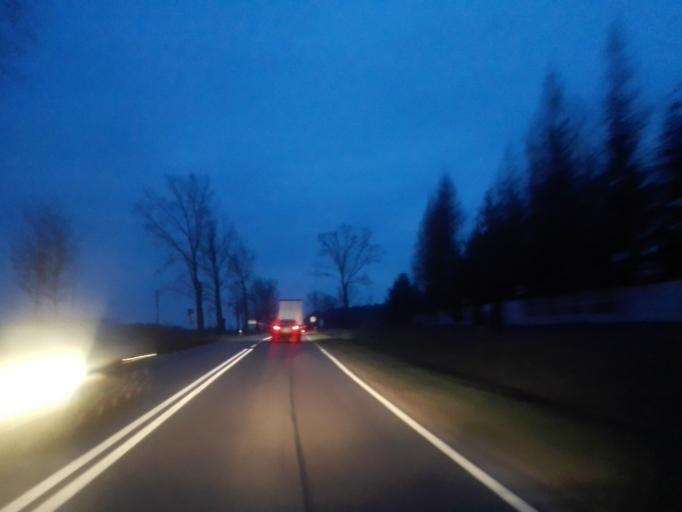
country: PL
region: Podlasie
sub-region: Lomza
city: Lomza
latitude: 53.1086
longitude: 22.0286
